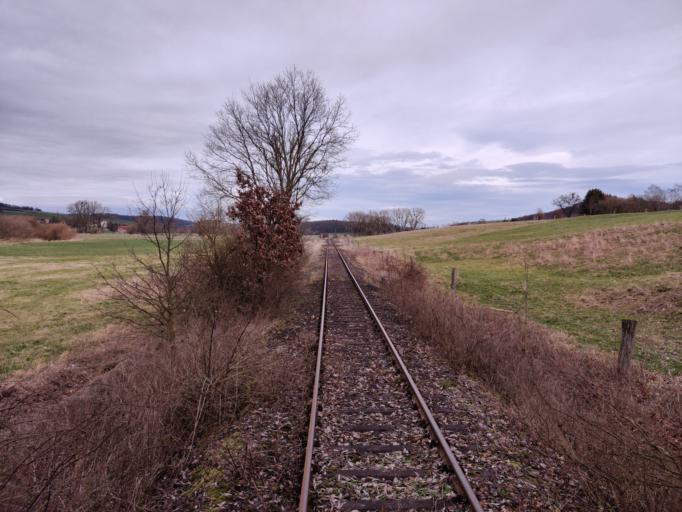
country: DE
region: Lower Saxony
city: Bockenem
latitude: 52.0472
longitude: 10.1286
